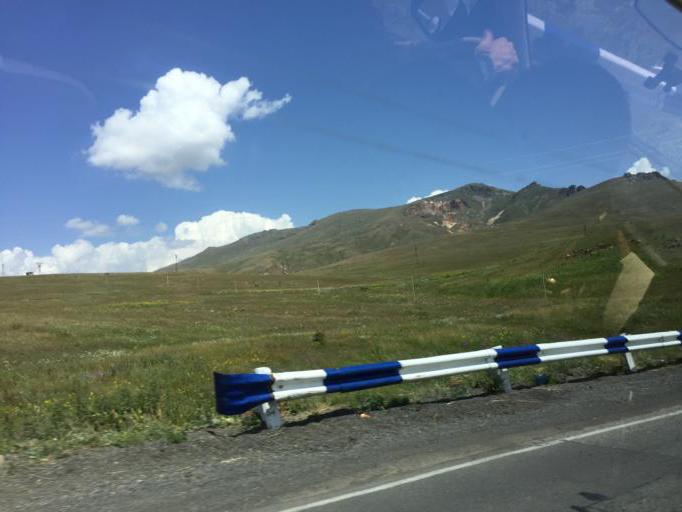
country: AM
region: Vayots' Dzori Marz
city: Jermuk
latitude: 39.6882
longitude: 45.7155
